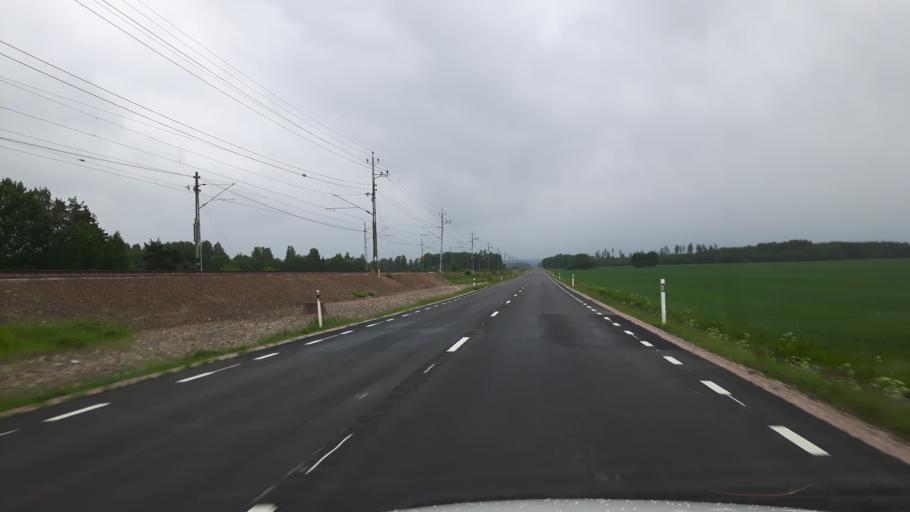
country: SE
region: Vaestmanland
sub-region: Kopings Kommun
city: Koping
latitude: 59.4346
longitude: 15.9383
